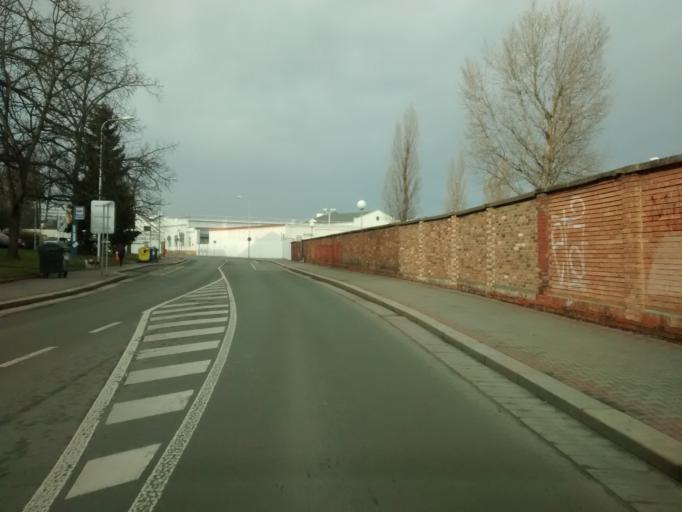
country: CZ
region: Central Bohemia
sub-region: Okres Mlada Boleslav
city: Mlada Boleslav
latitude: 50.4157
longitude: 14.9181
